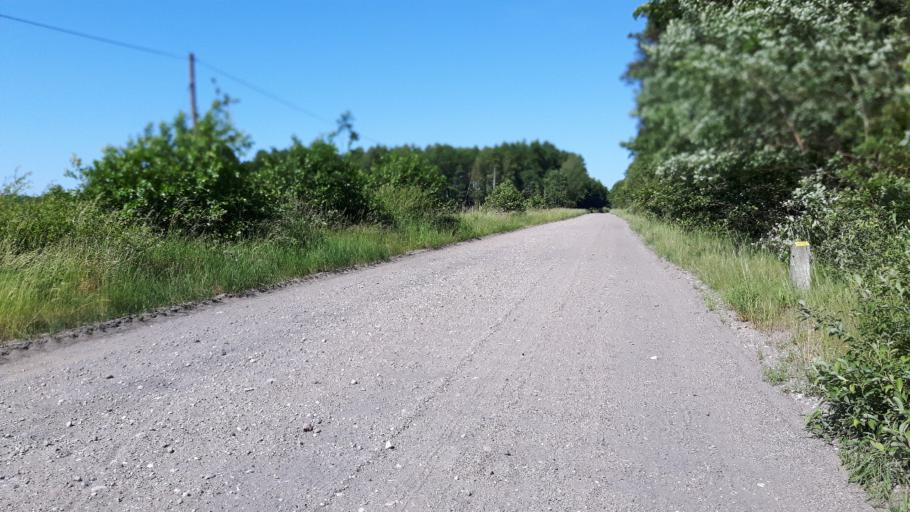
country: PL
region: Pomeranian Voivodeship
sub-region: Powiat slupski
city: Glowczyce
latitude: 54.6864
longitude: 17.4417
